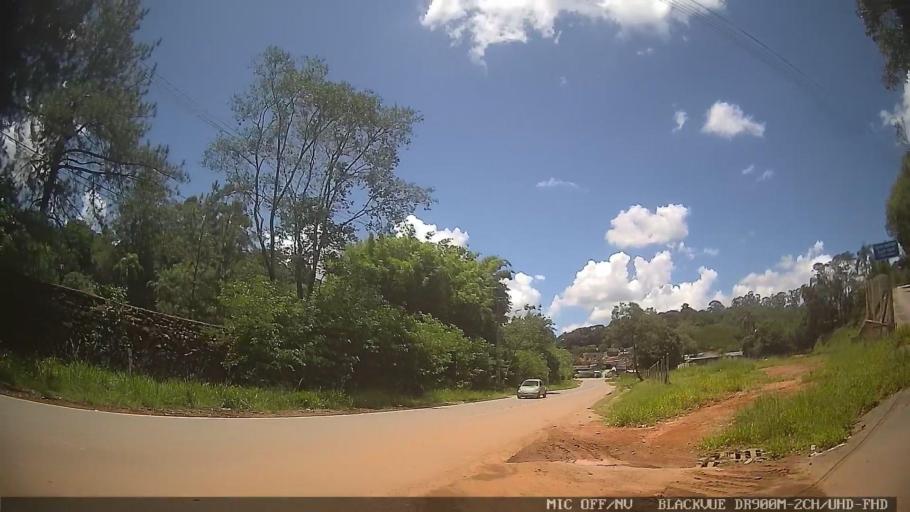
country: BR
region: Sao Paulo
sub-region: Piracaia
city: Piracaia
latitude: -23.0152
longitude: -46.4404
